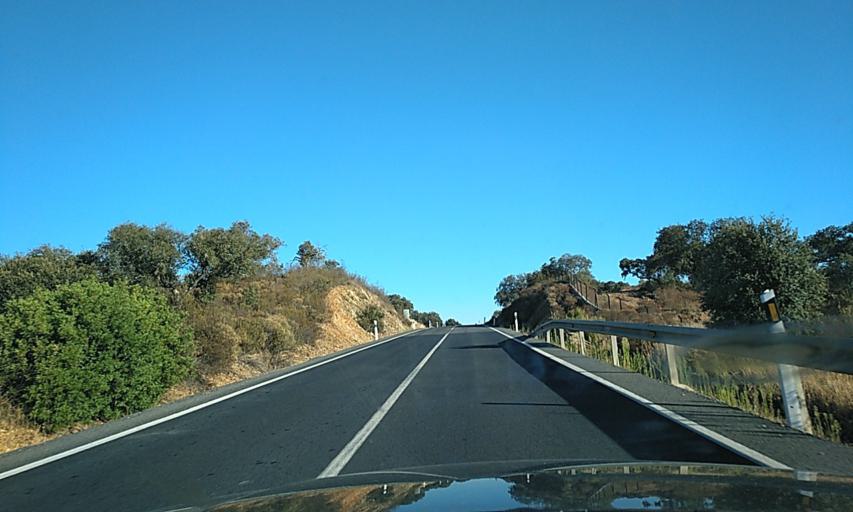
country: ES
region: Andalusia
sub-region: Provincia de Huelva
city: Alosno
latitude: 37.5221
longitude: -7.1354
